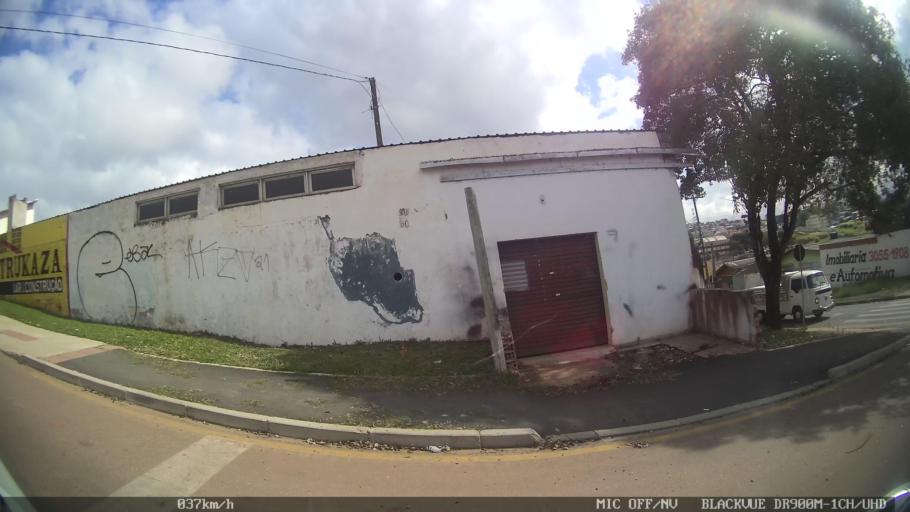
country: BR
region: Parana
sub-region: Pinhais
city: Pinhais
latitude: -25.3674
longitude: -49.1950
